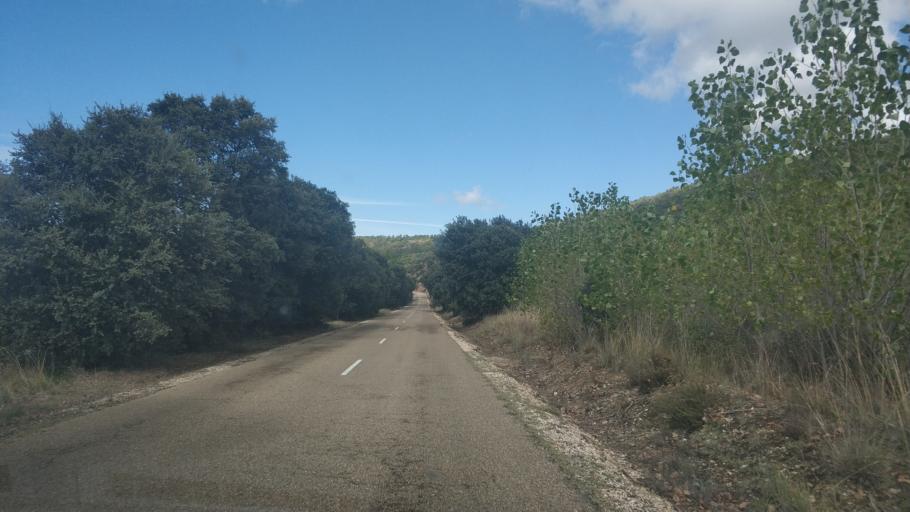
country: ES
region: Castille and Leon
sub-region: Provincia de Burgos
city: Retuerta
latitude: 42.0394
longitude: -3.4865
